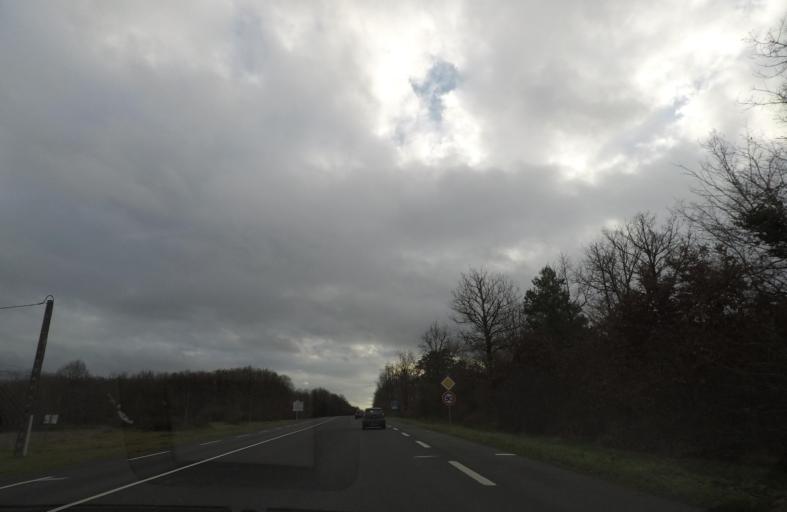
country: FR
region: Centre
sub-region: Departement du Loir-et-Cher
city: Soings-en-Sologne
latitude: 47.4551
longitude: 1.5287
